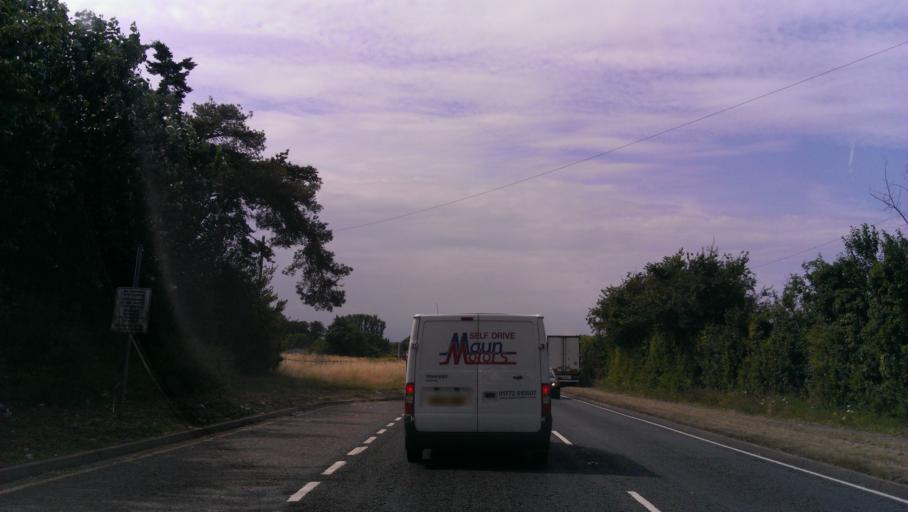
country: GB
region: England
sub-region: Kent
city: Teynham
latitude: 51.3201
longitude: 0.8298
